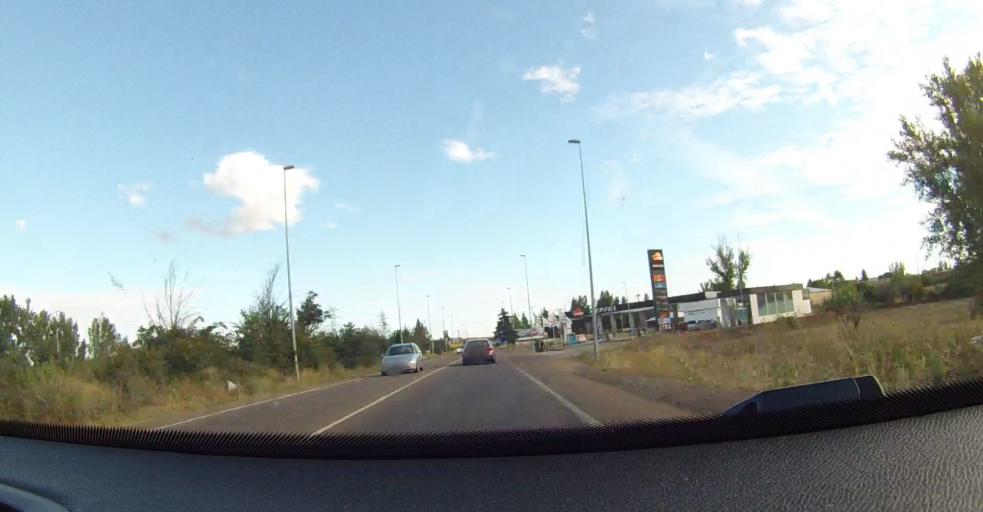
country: ES
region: Castille and Leon
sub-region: Provincia de Leon
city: Leon
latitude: 42.5718
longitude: -5.5832
